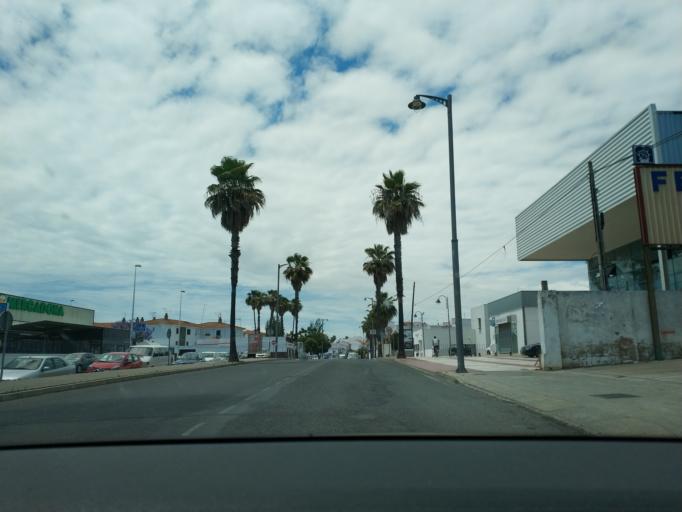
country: ES
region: Andalusia
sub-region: Provincia de Huelva
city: Cartaya
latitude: 37.2860
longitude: -7.1462
